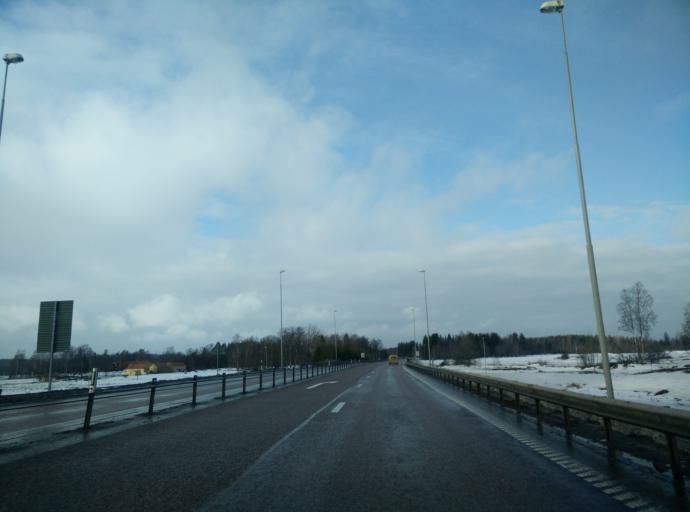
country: SE
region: Gaevleborg
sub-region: Sandvikens Kommun
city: Jarbo
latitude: 60.6100
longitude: 16.6411
